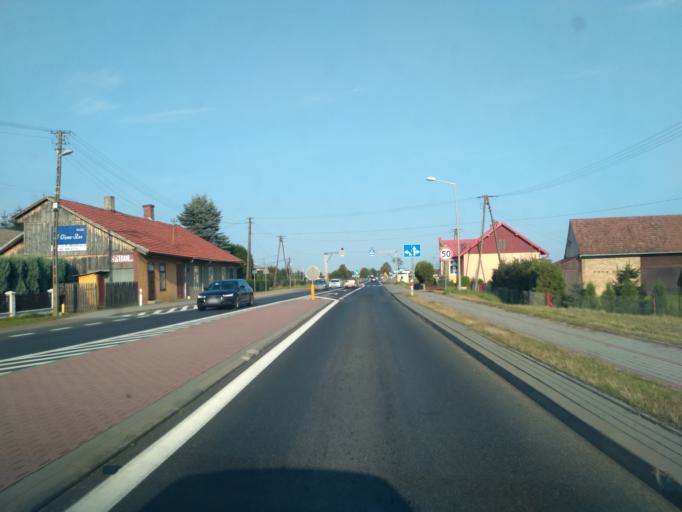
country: PL
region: Subcarpathian Voivodeship
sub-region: Powiat jasielski
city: Jaslo
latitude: 49.7592
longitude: 21.5273
